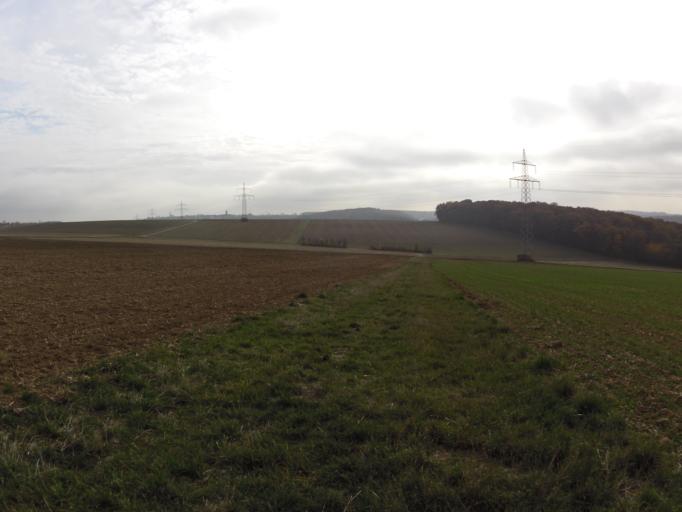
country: DE
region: Bavaria
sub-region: Regierungsbezirk Unterfranken
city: Waldbrunn
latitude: 49.7589
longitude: 9.8151
